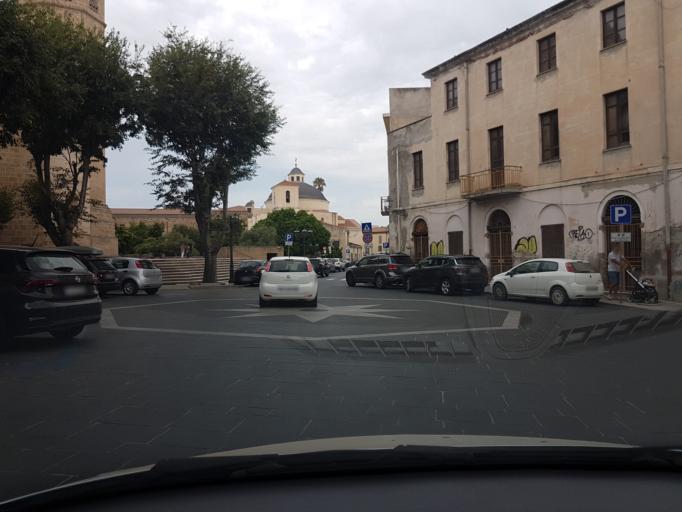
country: IT
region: Sardinia
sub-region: Provincia di Oristano
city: Oristano
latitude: 39.9027
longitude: 8.5911
